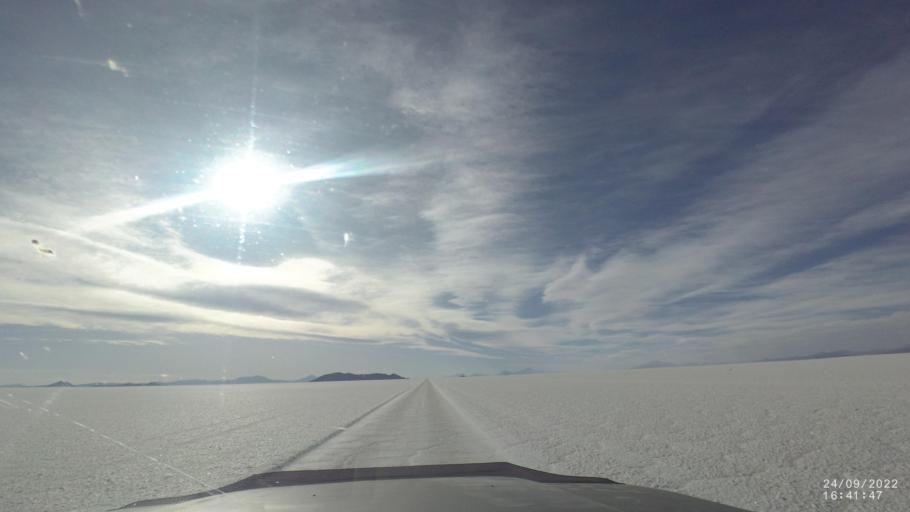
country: BO
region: Potosi
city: Colchani
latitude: -20.1817
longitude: -67.7211
